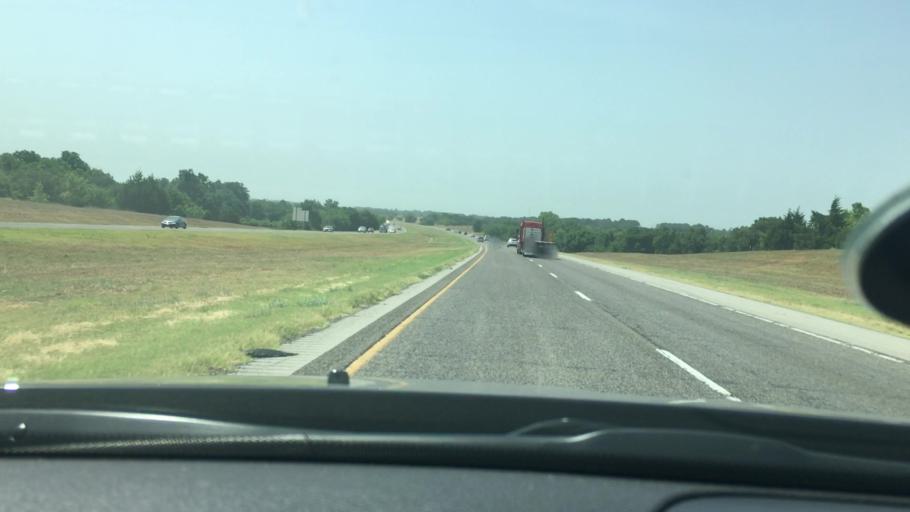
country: US
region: Oklahoma
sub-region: Garvin County
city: Wynnewood
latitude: 34.6068
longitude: -97.2122
